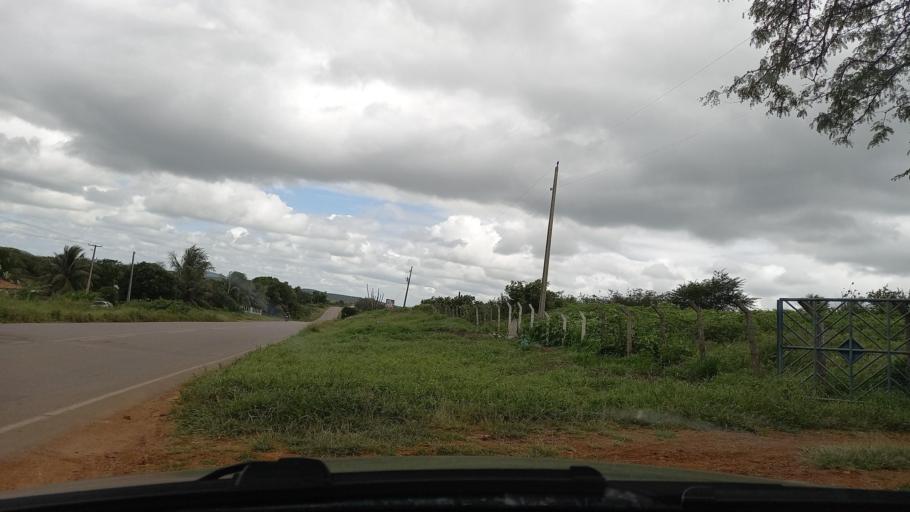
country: BR
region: Sergipe
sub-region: Caninde De Sao Francisco
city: Caninde de Sao Francisco
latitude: -9.6836
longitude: -37.8128
